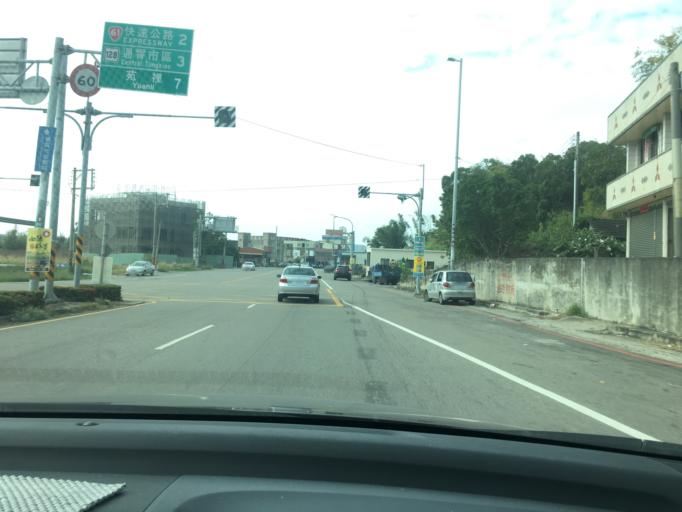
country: TW
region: Taiwan
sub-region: Miaoli
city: Miaoli
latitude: 24.4970
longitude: 120.7038
